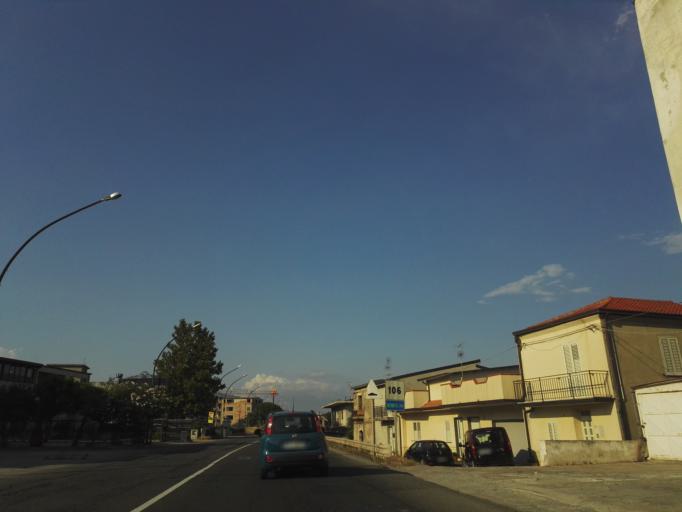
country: IT
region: Calabria
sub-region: Provincia di Reggio Calabria
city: Siderno
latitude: 38.2849
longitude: 16.3136
